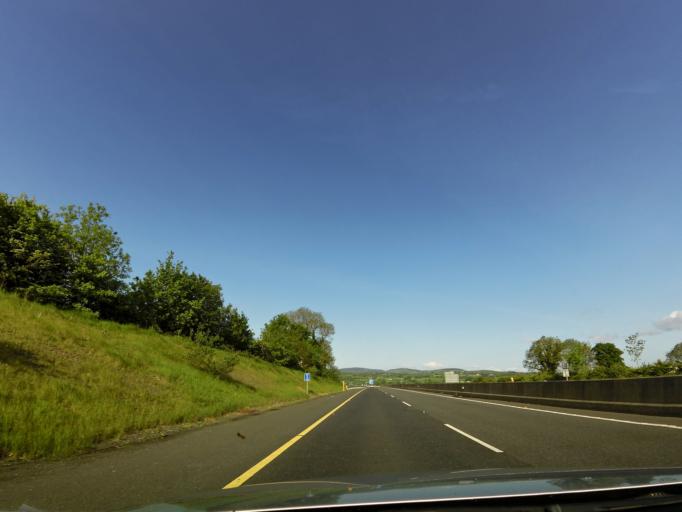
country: IE
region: Munster
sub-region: North Tipperary
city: Nenagh
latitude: 52.8444
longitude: -8.2296
